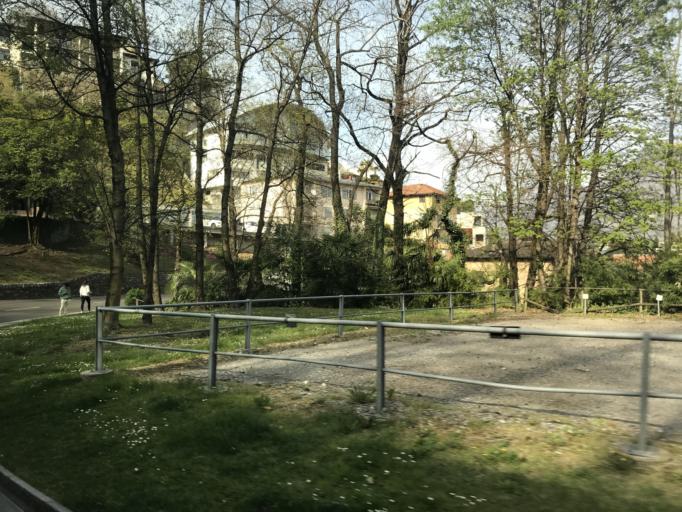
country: CH
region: Ticino
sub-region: Lugano District
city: Sorengo
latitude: 46.0008
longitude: 8.9396
